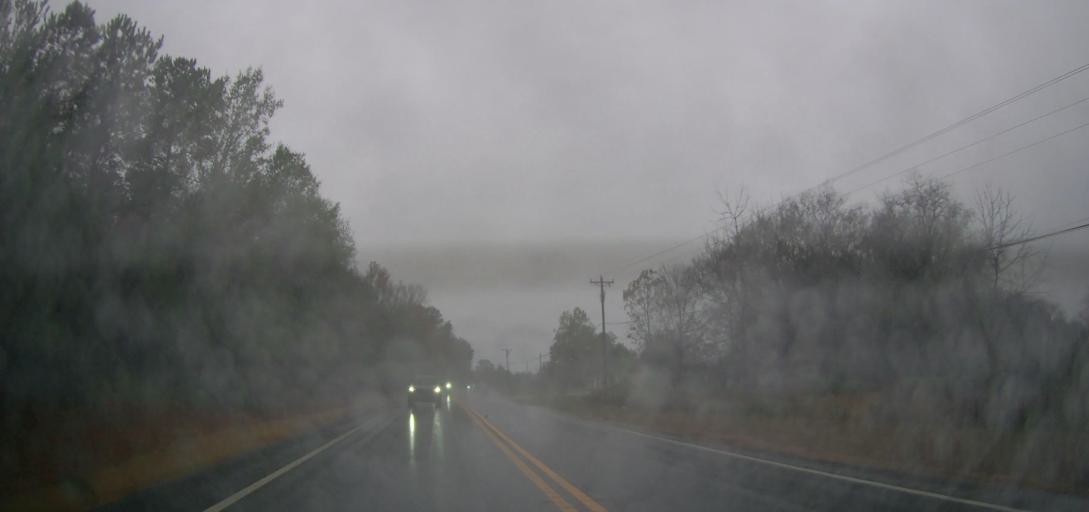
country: US
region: Georgia
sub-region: Putnam County
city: Eatonton
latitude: 33.2894
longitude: -83.3900
